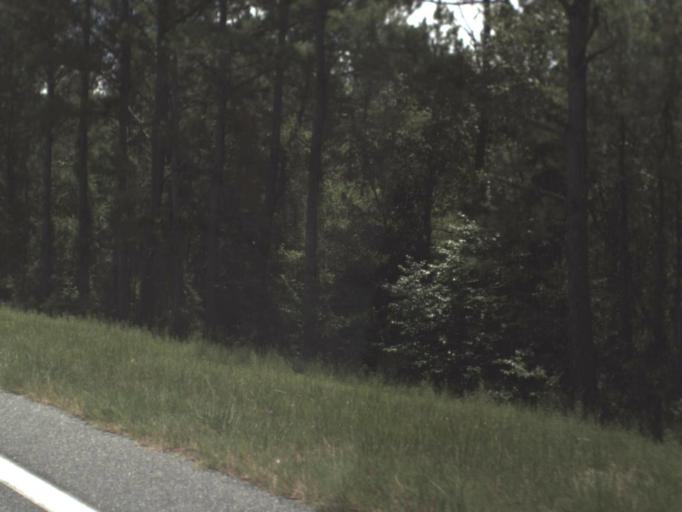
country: US
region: Florida
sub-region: Suwannee County
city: Wellborn
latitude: 30.3204
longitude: -82.7790
